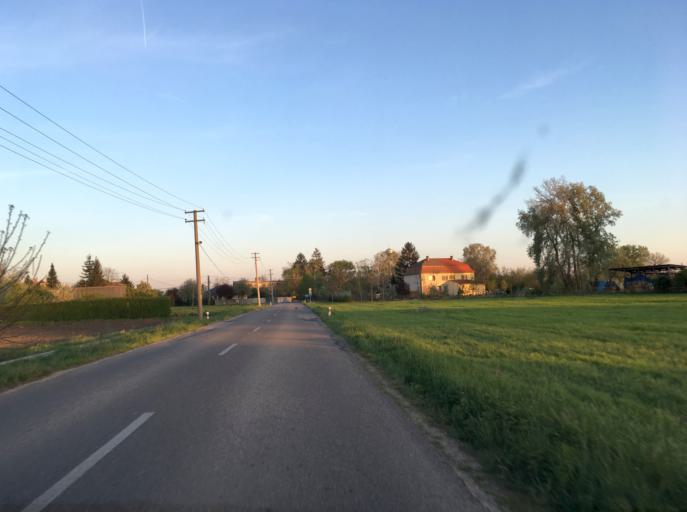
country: SK
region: Nitriansky
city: Kolarovo
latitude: 47.8900
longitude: 17.8961
